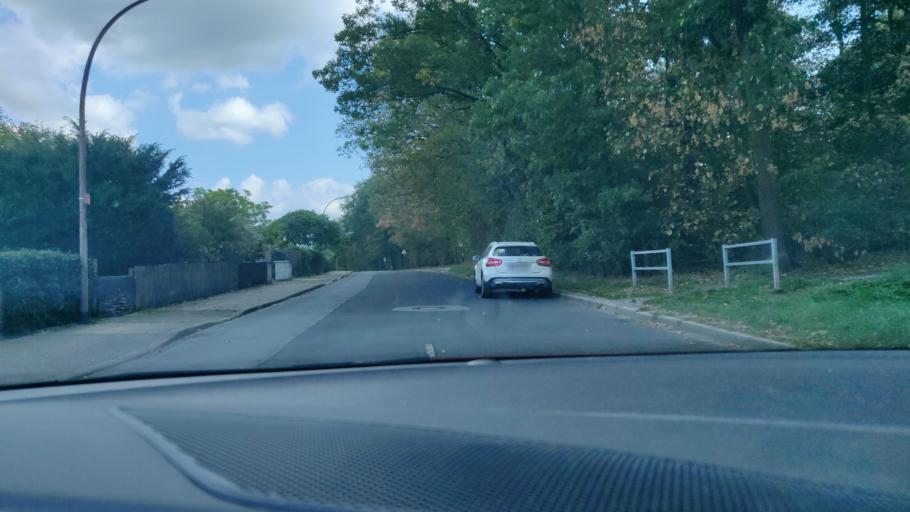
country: DE
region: North Rhine-Westphalia
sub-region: Regierungsbezirk Dusseldorf
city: Velbert
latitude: 51.3559
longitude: 7.0372
